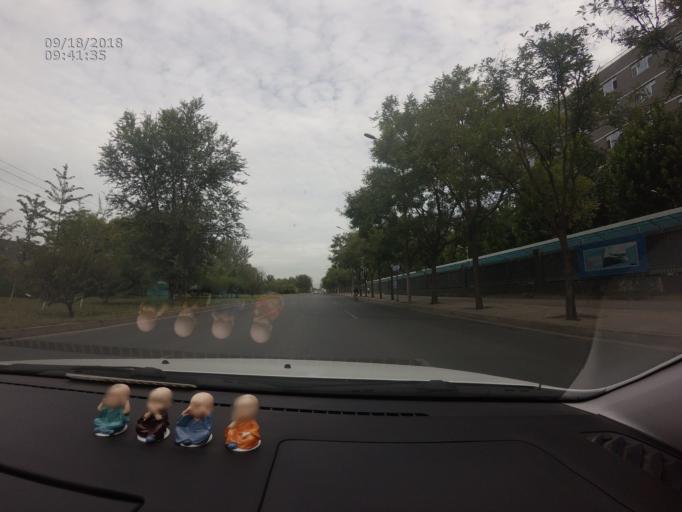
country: CN
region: Beijing
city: Xibeiwang
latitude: 40.0680
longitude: 116.2407
